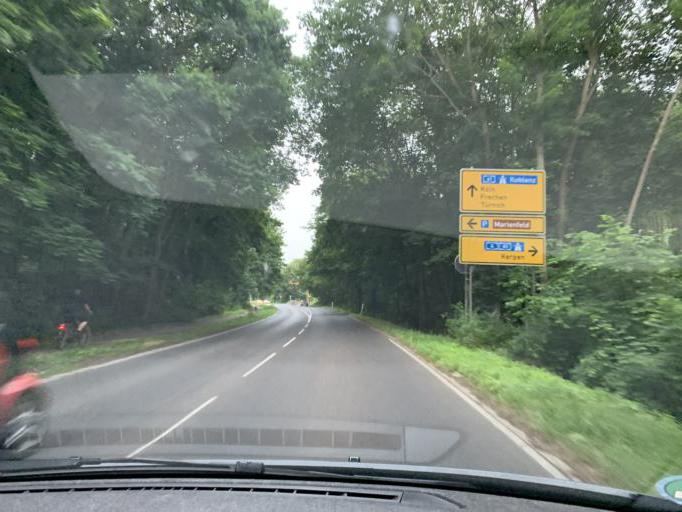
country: DE
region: North Rhine-Westphalia
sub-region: Regierungsbezirk Koln
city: Kerpen
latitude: 50.8855
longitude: 6.7181
